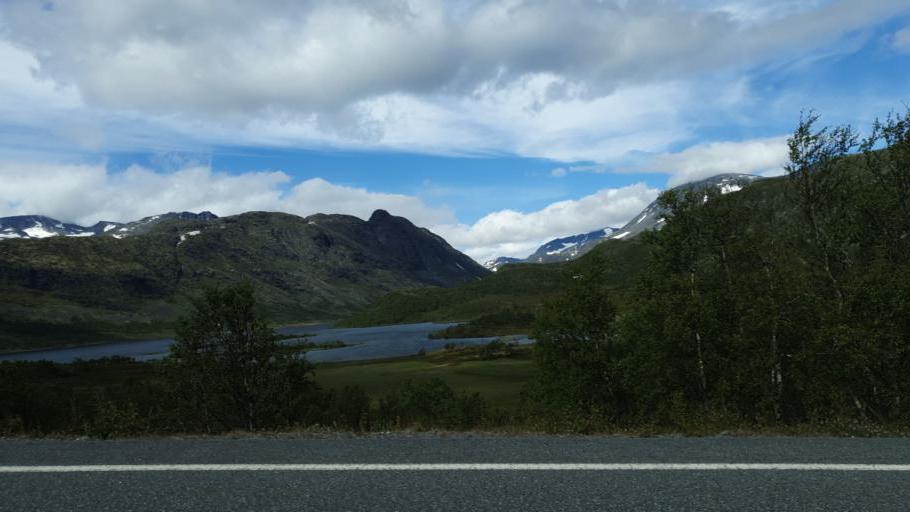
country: NO
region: Oppland
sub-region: Oystre Slidre
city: Heggenes
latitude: 61.4765
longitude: 8.8227
